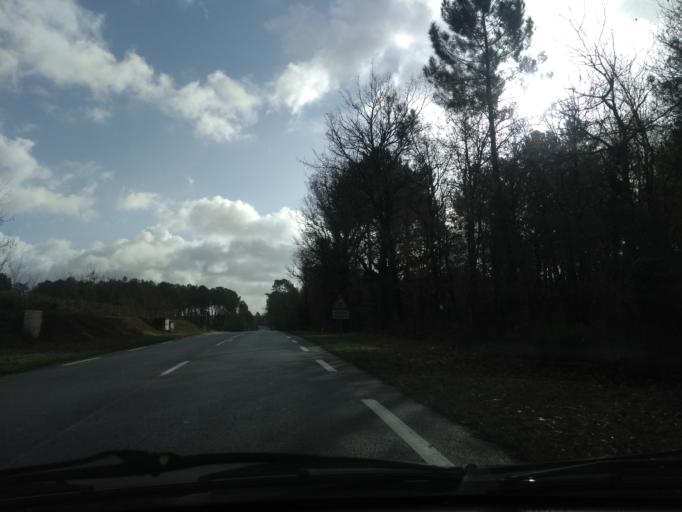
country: FR
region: Aquitaine
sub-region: Departement de la Gironde
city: Salles
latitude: 44.5393
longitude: -0.8459
